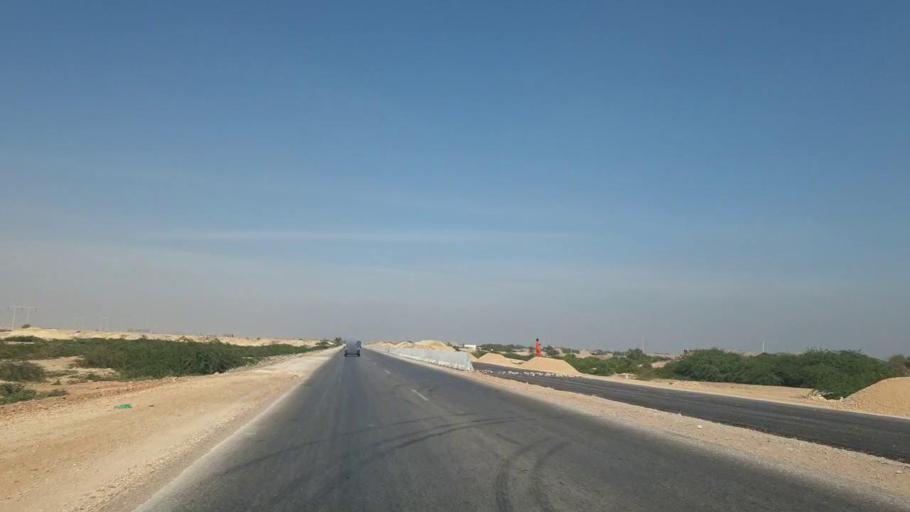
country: PK
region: Sindh
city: Matiari
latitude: 25.6672
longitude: 68.2955
